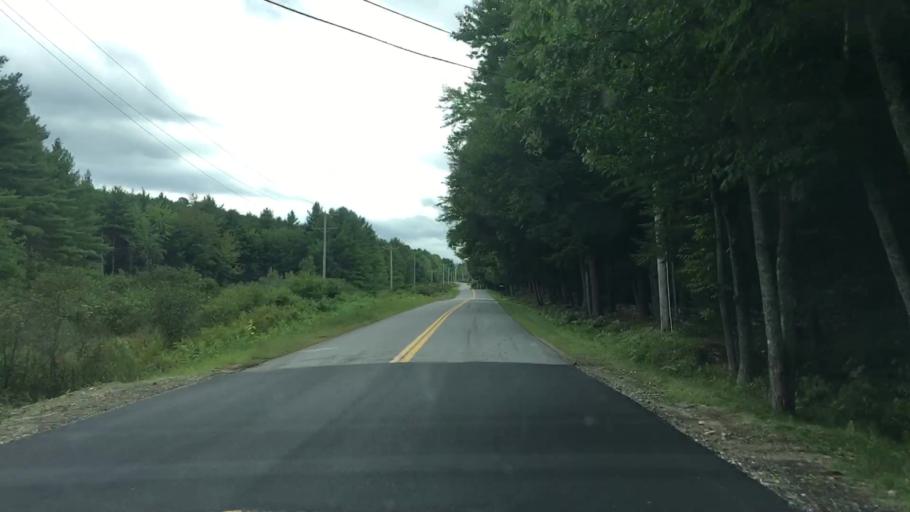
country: US
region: Maine
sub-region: Kennebec County
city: Hallowell
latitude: 44.2712
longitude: -69.8123
